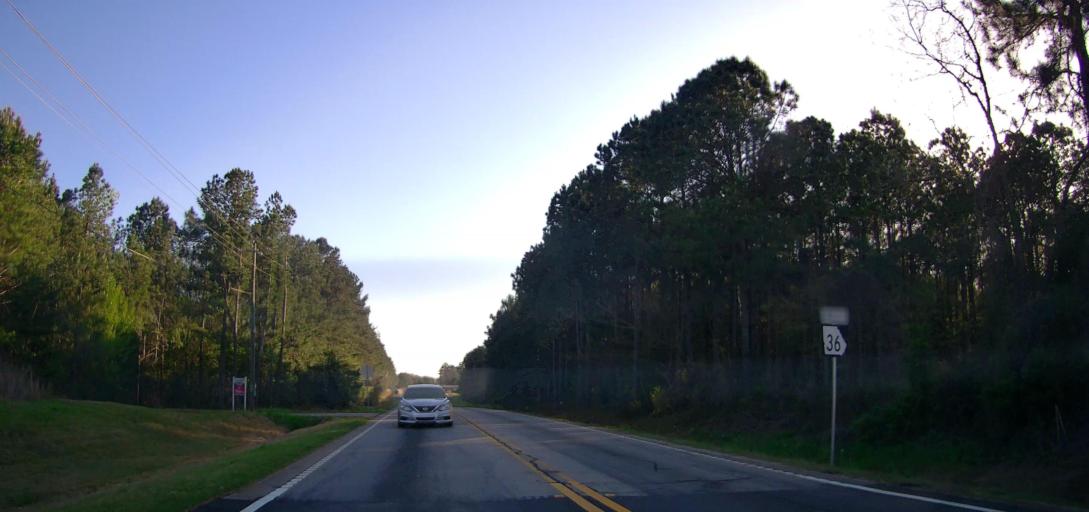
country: US
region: Georgia
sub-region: Butts County
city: Jackson
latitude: 33.3830
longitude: -83.9038
